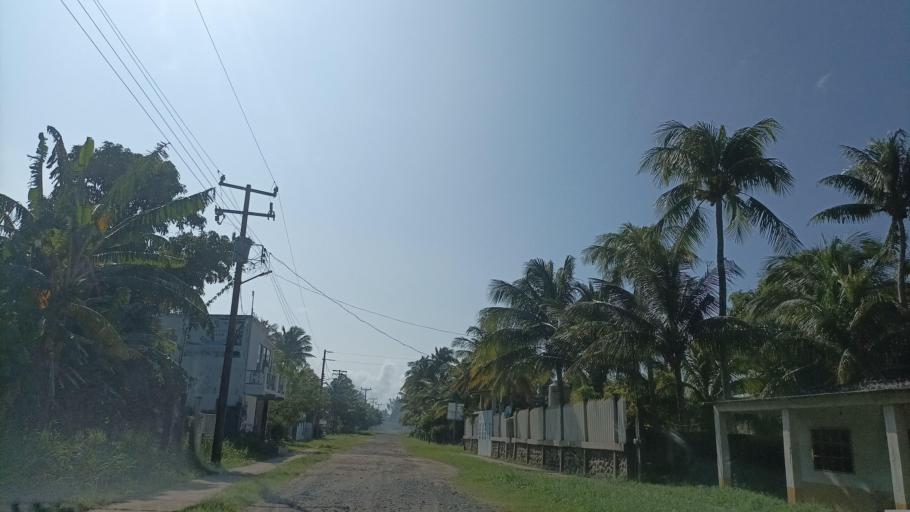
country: MX
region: Veracruz
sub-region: Coatzacoalcos
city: Fraccionamiento Ciudad Olmeca
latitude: 18.2115
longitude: -94.6113
